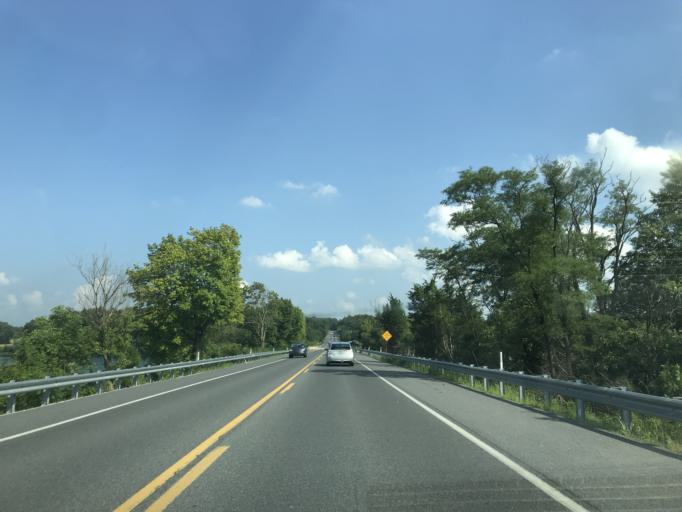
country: US
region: Pennsylvania
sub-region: York County
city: Parkville
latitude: 39.7891
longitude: -76.9178
